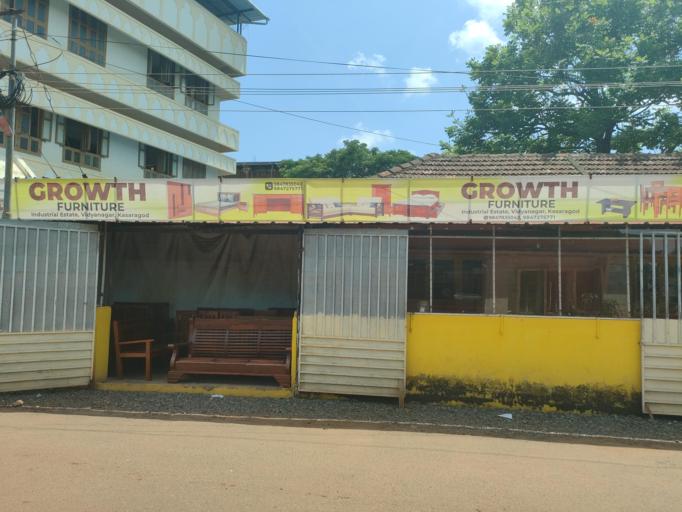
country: IN
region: Kerala
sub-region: Kasaragod District
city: Kasaragod
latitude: 12.5186
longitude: 75.0162
